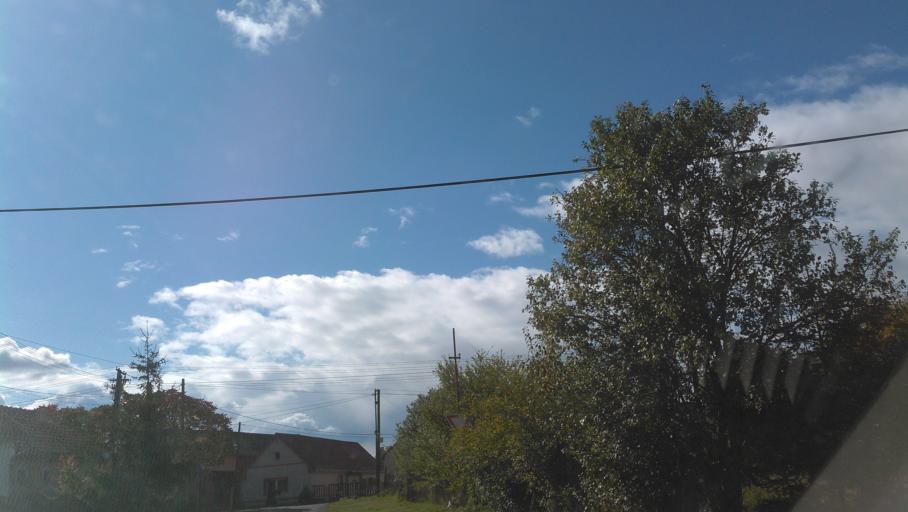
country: SK
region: Banskobystricky
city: Poltar
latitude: 48.3814
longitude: 19.8938
